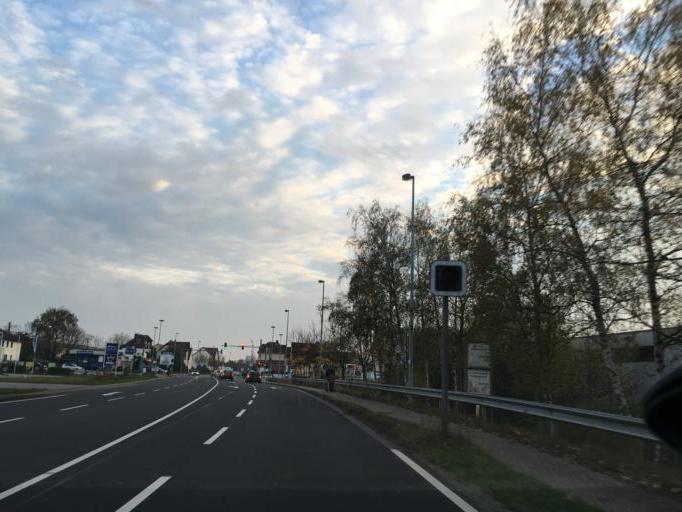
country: DE
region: Lower Saxony
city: Celle
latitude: 52.6397
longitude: 10.0782
